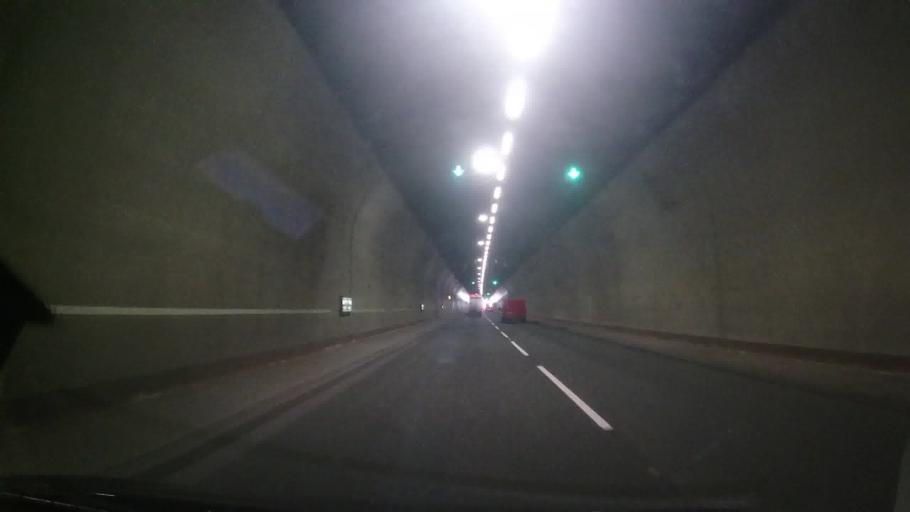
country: GB
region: Wales
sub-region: Conwy
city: Llanfairfechan
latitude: 53.2657
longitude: -3.9504
